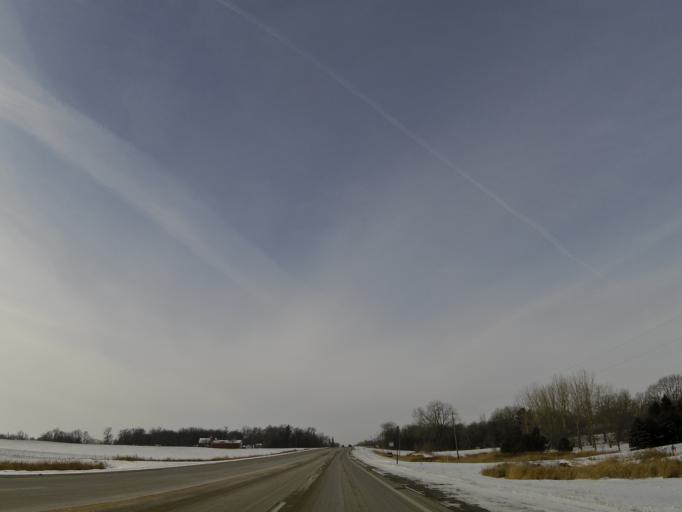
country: US
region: Minnesota
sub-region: McLeod County
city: Hutchinson
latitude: 44.8925
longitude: -94.2608
